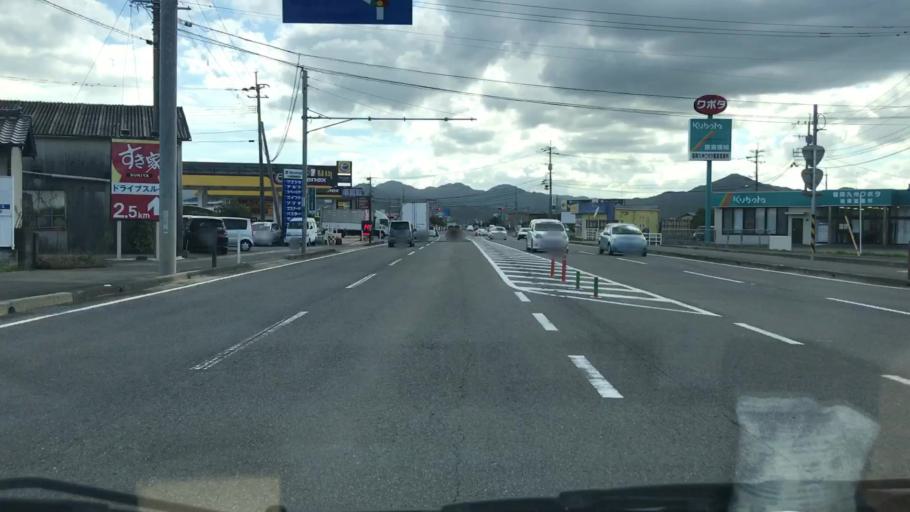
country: JP
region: Saga Prefecture
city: Kashima
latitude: 33.1283
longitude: 130.1048
